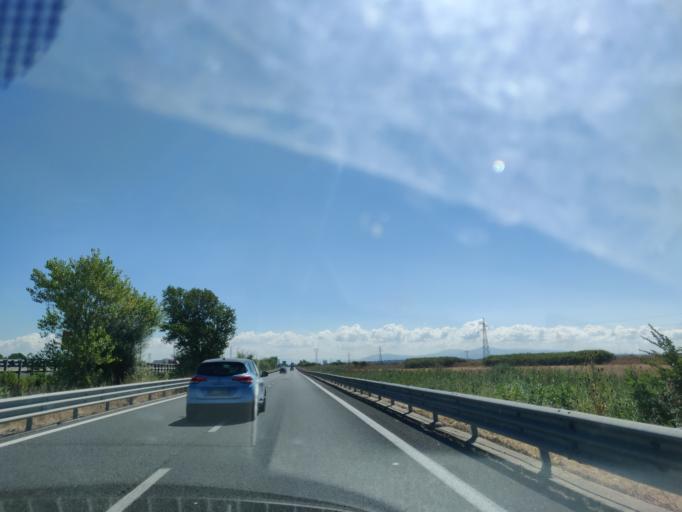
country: IT
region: Latium
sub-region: Citta metropolitana di Roma Capitale
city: Ponte Galeria-La Pisana
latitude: 41.8148
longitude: 12.3553
